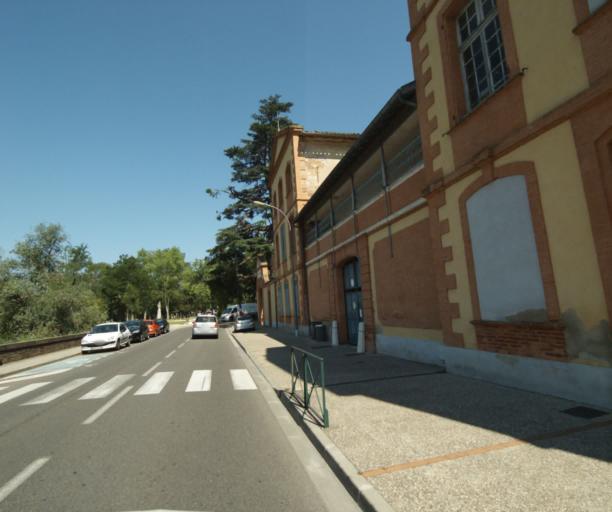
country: FR
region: Midi-Pyrenees
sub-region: Departement du Tarn-et-Garonne
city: Montauban
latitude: 44.0216
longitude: 1.3483
